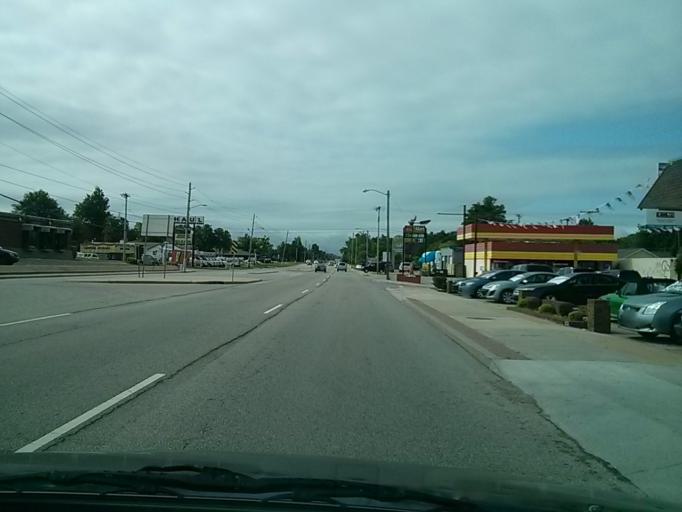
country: US
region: Oklahoma
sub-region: Tulsa County
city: Tulsa
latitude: 36.1162
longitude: -95.9225
